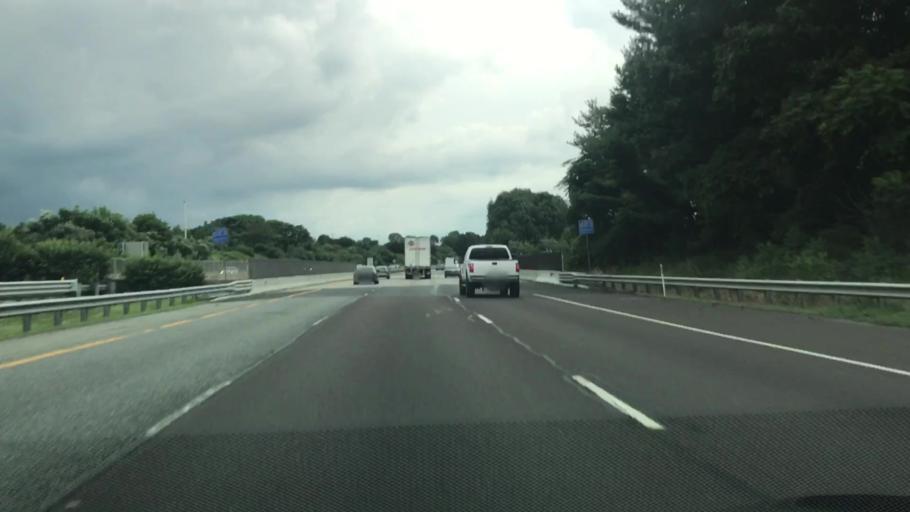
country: US
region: New Jersey
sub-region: Warren County
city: Alpha
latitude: 40.6523
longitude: -75.1535
